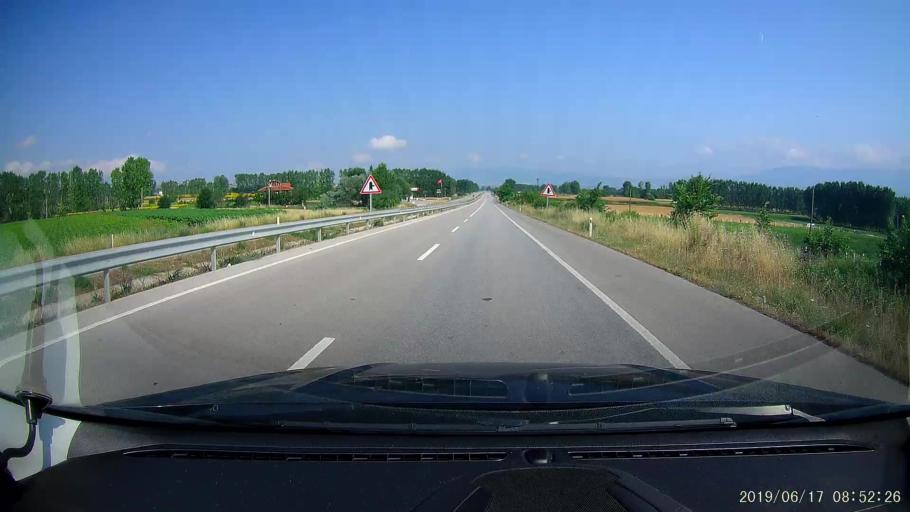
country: TR
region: Tokat
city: Erbaa
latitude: 40.6977
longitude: 36.4967
